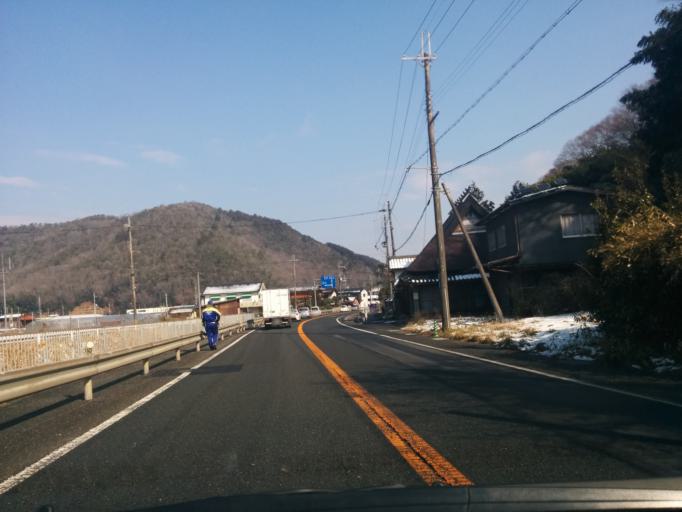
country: JP
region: Kyoto
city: Kameoka
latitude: 35.1378
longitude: 135.4255
